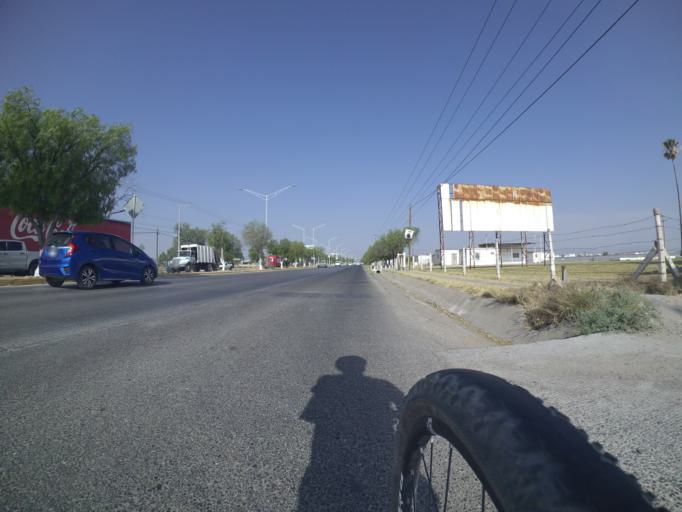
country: MX
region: Aguascalientes
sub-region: Jesus Maria
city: El Llano
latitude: 21.9480
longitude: -102.3083
